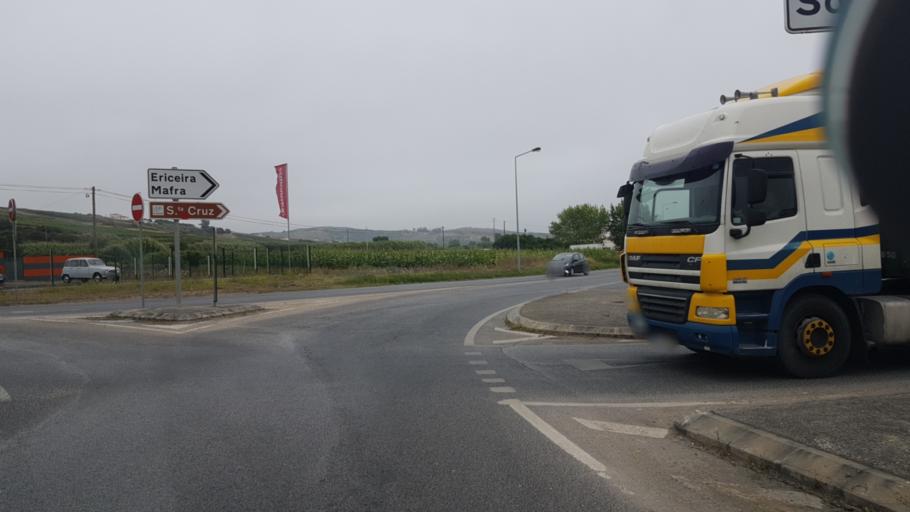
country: PT
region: Lisbon
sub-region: Torres Vedras
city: Torres Vedras
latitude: 39.0963
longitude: -9.2901
